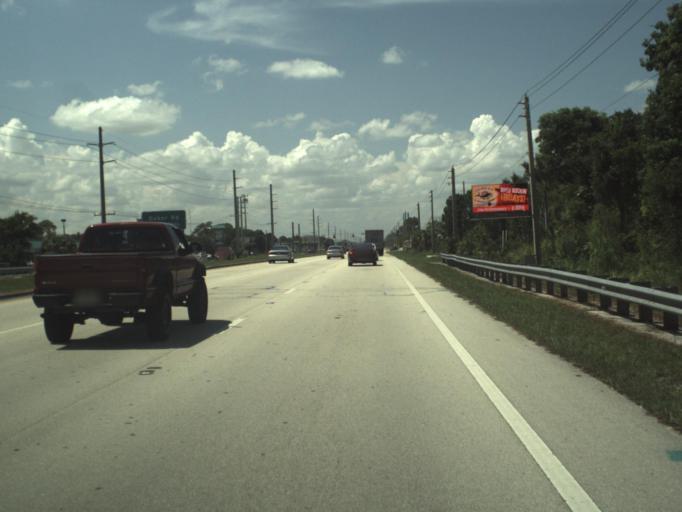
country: US
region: Florida
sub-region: Martin County
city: North River Shores
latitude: 27.2192
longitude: -80.2622
